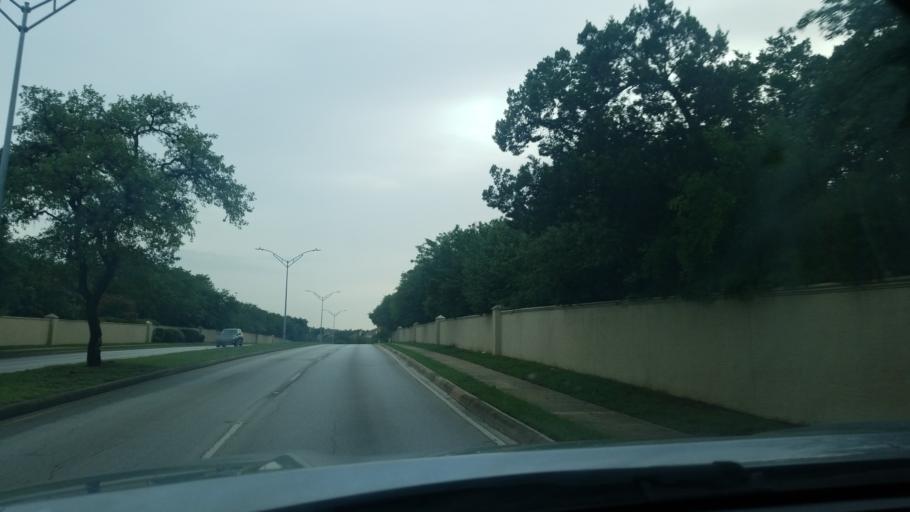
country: US
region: Texas
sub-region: Bexar County
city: Hollywood Park
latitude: 29.6147
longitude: -98.5190
